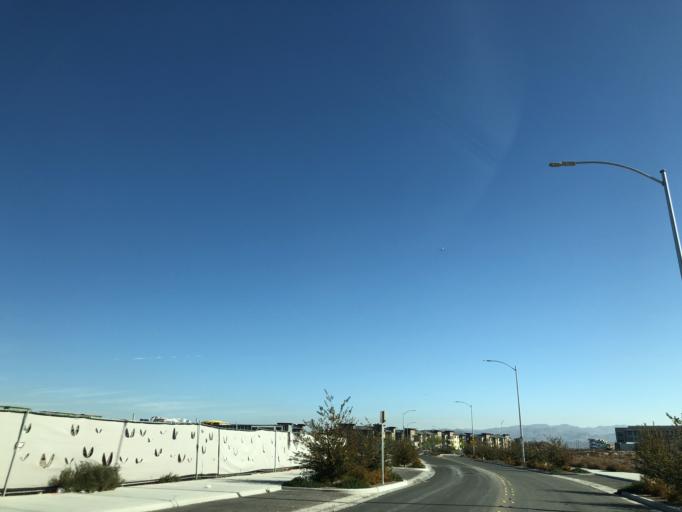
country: US
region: Nevada
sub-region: Clark County
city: Whitney
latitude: 36.0760
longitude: -115.0347
